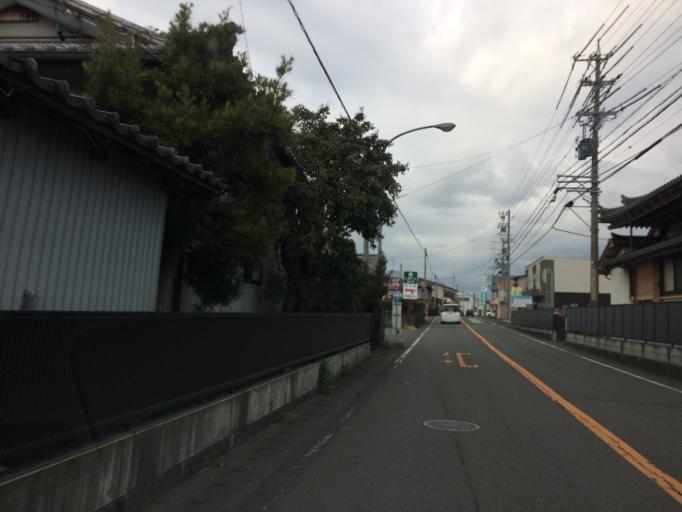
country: JP
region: Shizuoka
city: Shizuoka-shi
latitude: 34.9412
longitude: 138.3584
